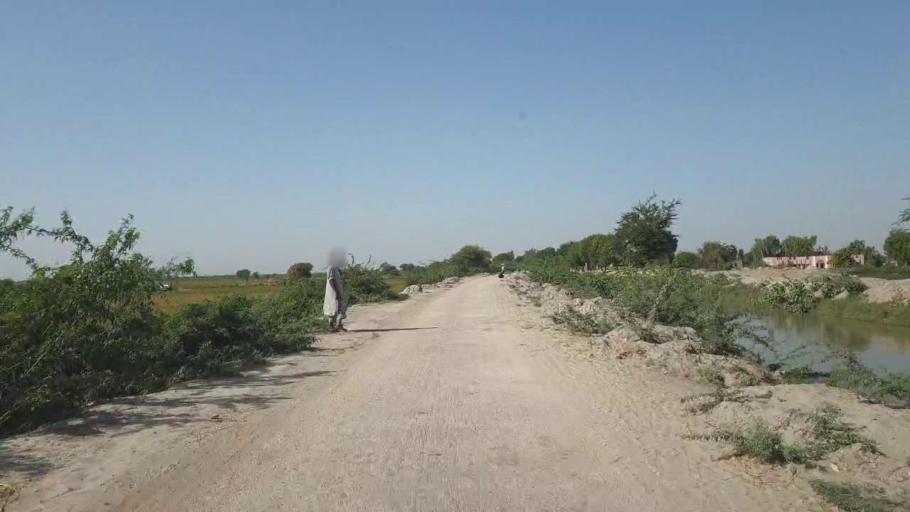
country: PK
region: Sindh
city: Kadhan
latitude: 24.5737
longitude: 68.9860
